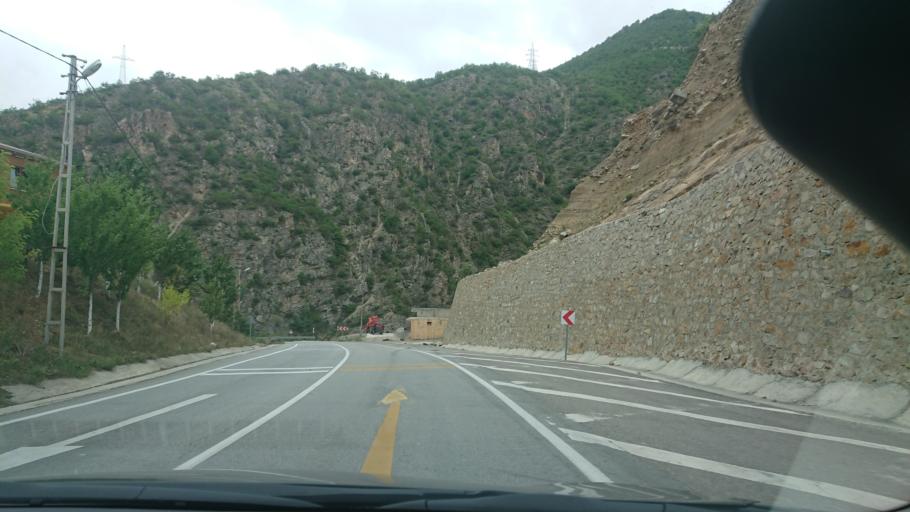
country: TR
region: Gumushane
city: Kurtun
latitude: 40.7042
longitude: 39.0796
